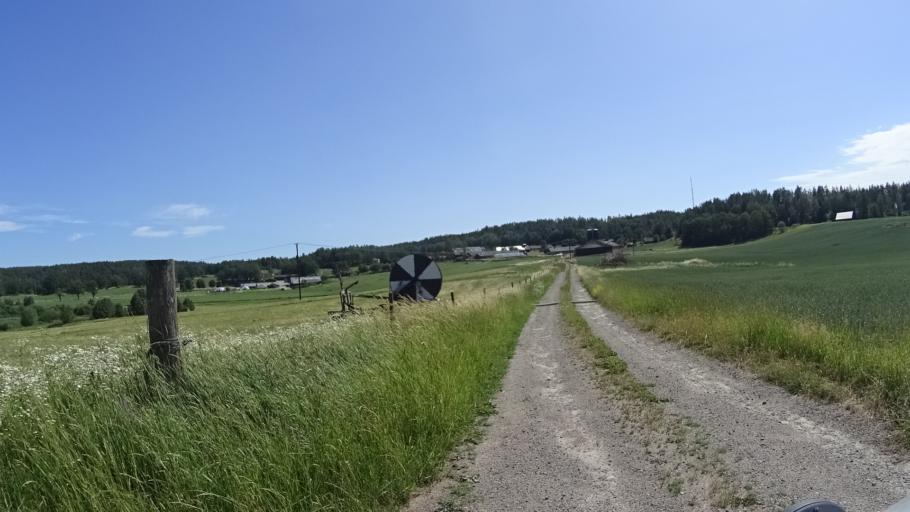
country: SE
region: Kalmar
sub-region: Vasterviks Kommun
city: Gamleby
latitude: 57.9186
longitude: 16.4066
